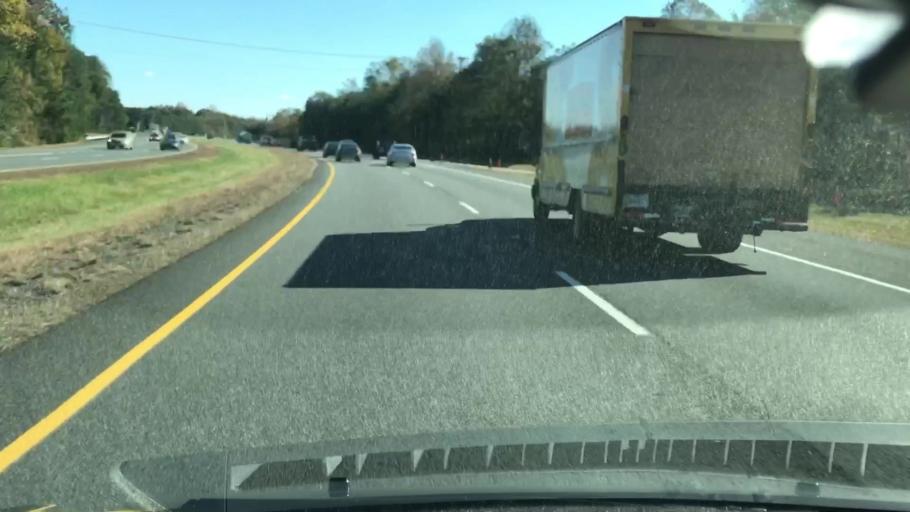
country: US
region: Virginia
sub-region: Fairfax County
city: Fairfax Station
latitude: 38.7871
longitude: -77.3236
